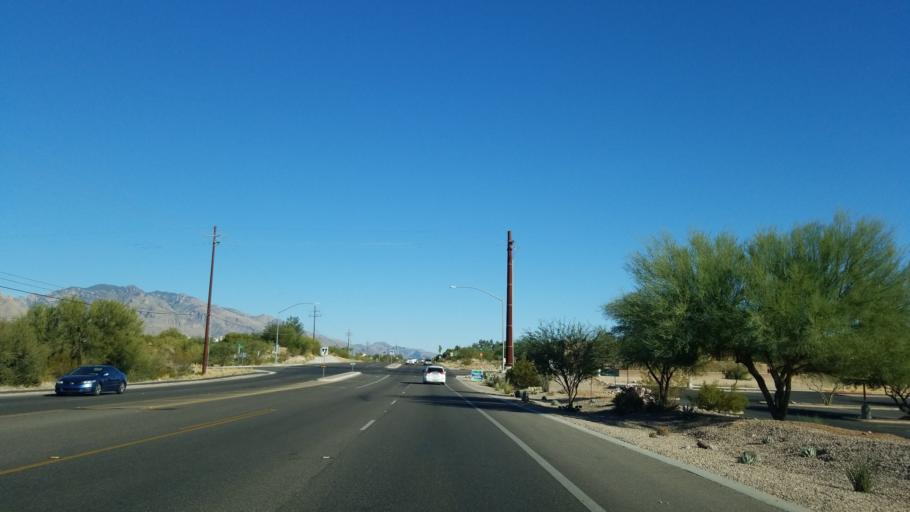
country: US
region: Arizona
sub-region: Pima County
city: Casas Adobes
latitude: 32.3231
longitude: -111.0219
